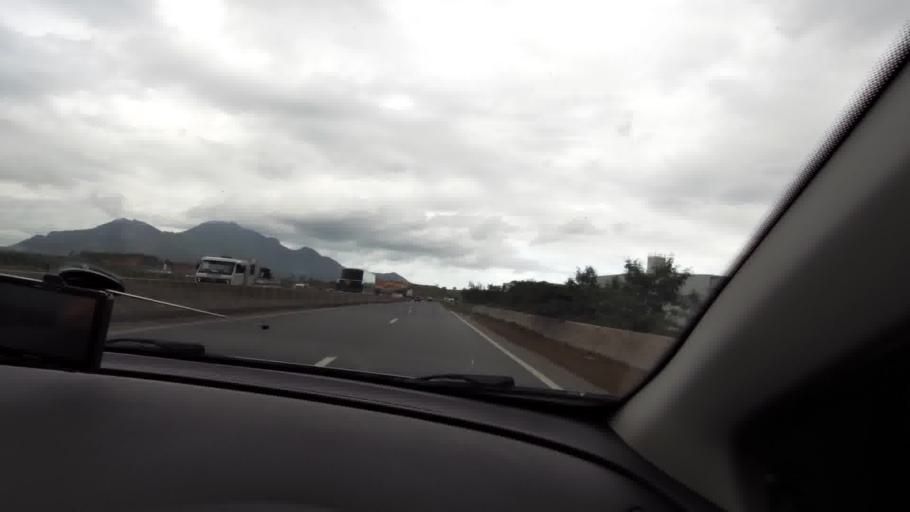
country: BR
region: Espirito Santo
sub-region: Vitoria
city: Vitoria
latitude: -20.2253
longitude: -40.3614
